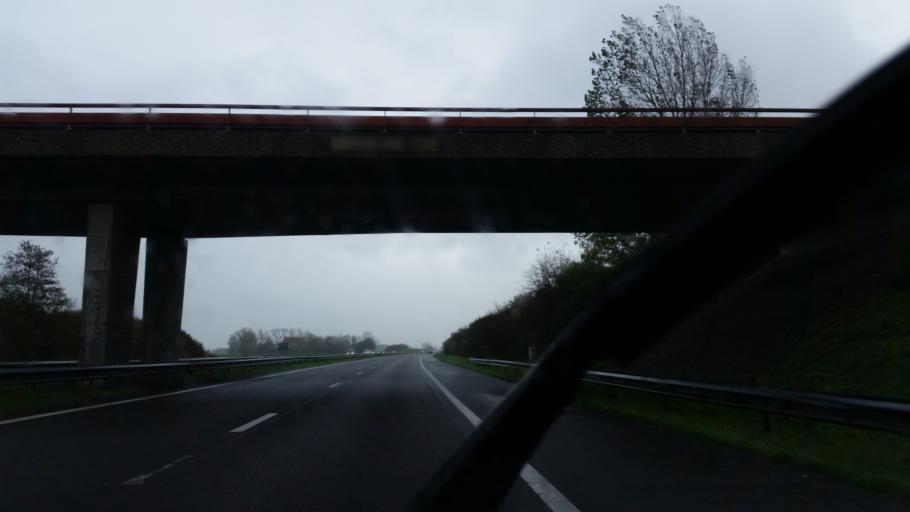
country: NL
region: Friesland
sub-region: Gemeente Boarnsterhim
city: Reduzum
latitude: 53.1120
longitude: 5.8129
